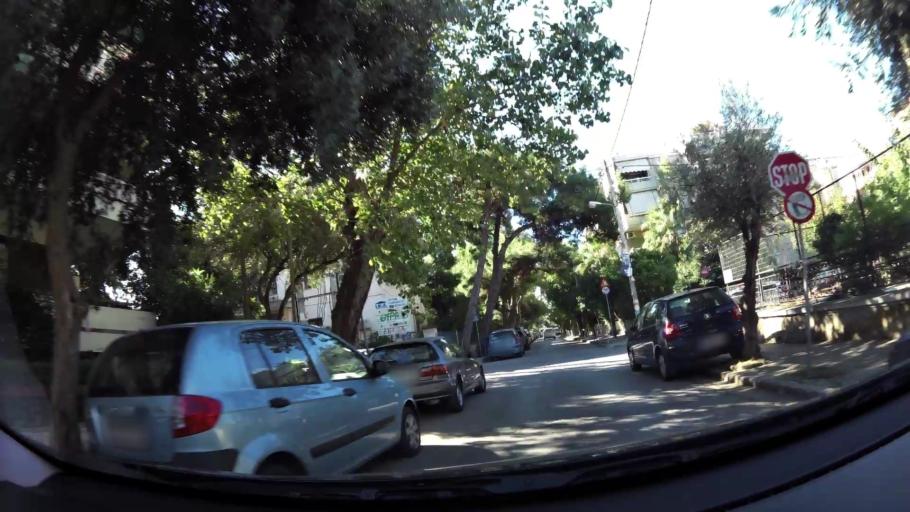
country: GR
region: Attica
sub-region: Nomarchia Athinas
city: Khalandrion
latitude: 38.0233
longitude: 23.8058
